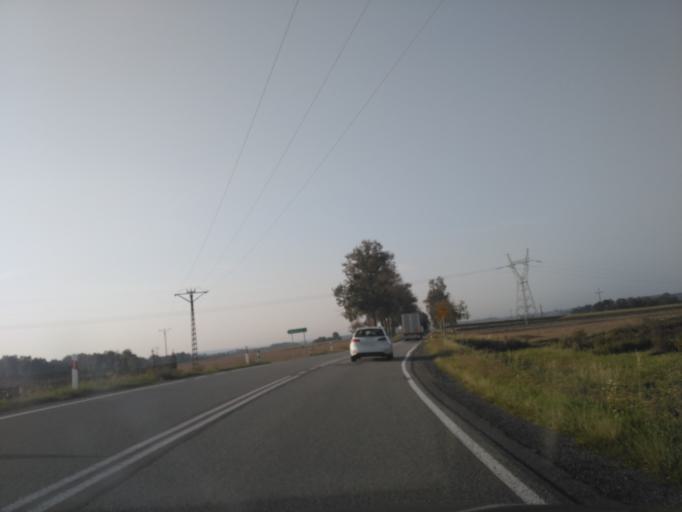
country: PL
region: Lublin Voivodeship
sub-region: Powiat krasnicki
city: Szastarka
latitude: 50.8161
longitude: 22.3190
